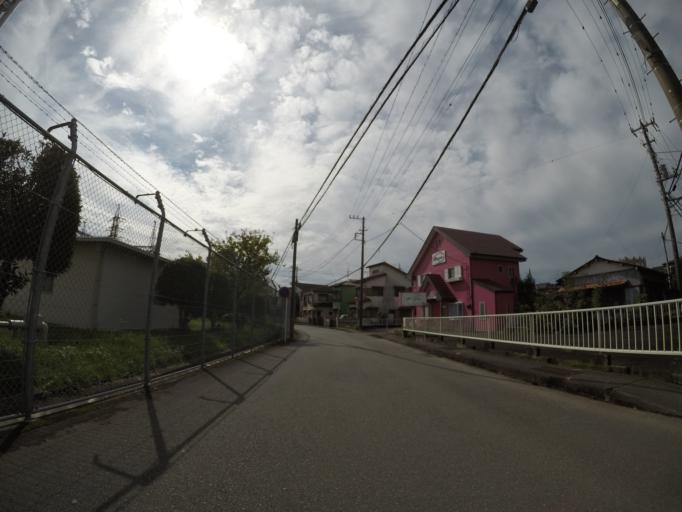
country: JP
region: Shizuoka
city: Fuji
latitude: 35.1764
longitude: 138.6909
